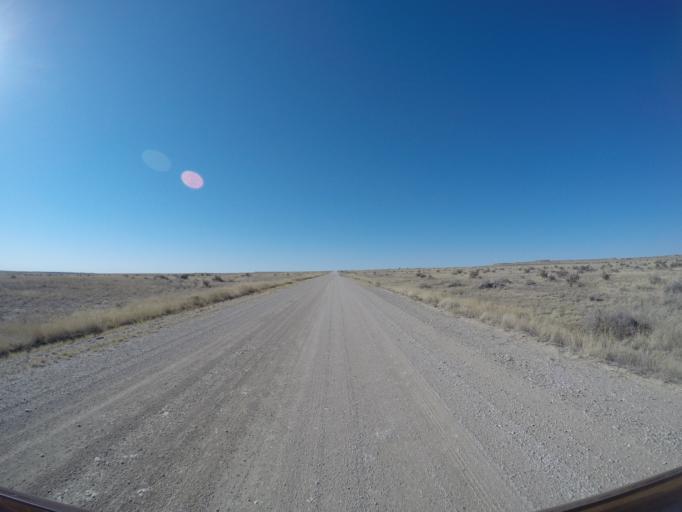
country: US
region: Colorado
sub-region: Otero County
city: La Junta
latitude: 37.8016
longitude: -103.5000
